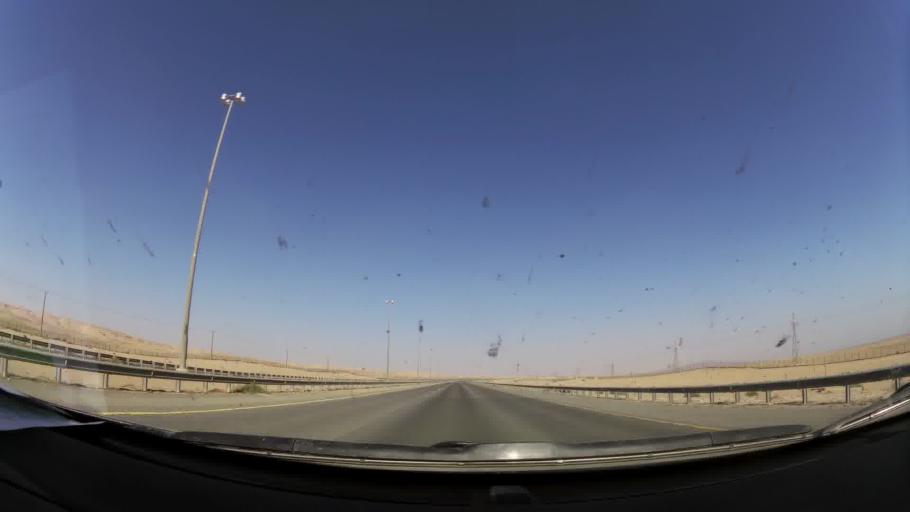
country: KW
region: Muhafazat al Jahra'
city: Al Jahra'
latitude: 29.5089
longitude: 47.8007
